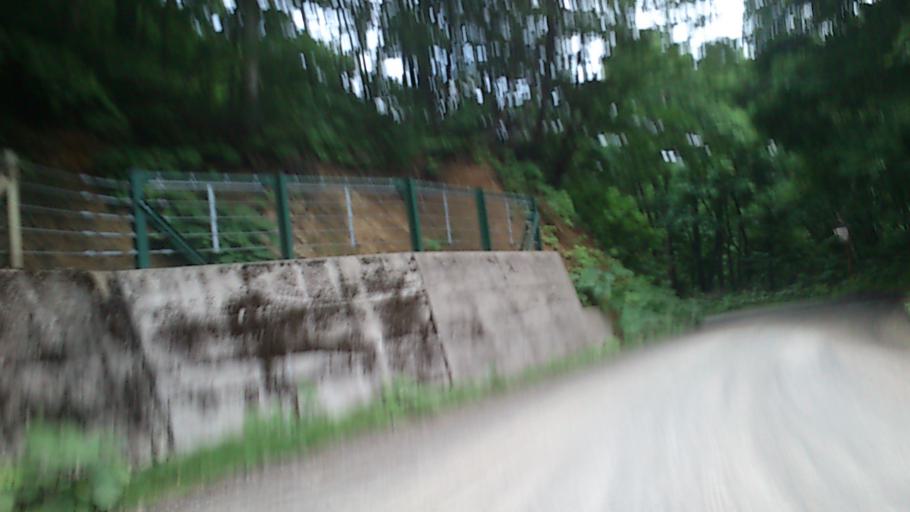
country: JP
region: Aomori
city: Hirosaki
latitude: 40.5374
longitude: 140.1839
